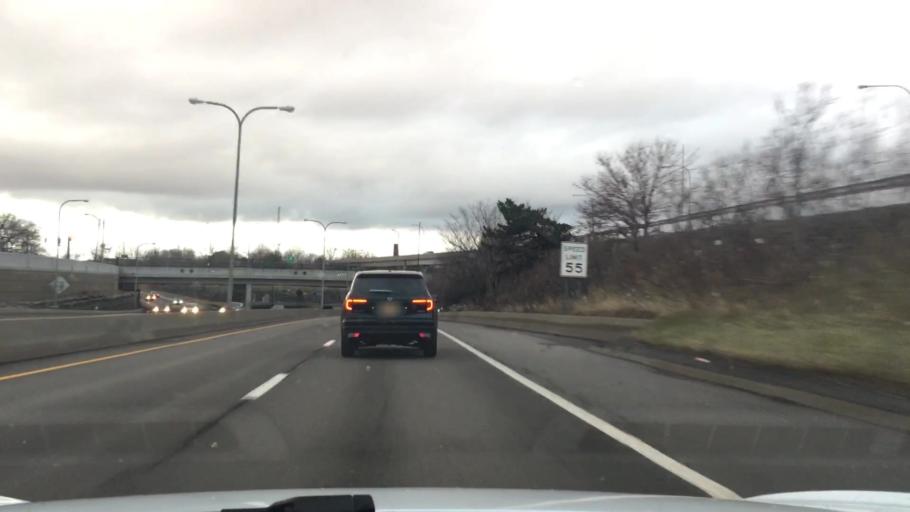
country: US
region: New York
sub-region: Erie County
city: Buffalo
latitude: 42.9206
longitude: -78.8432
